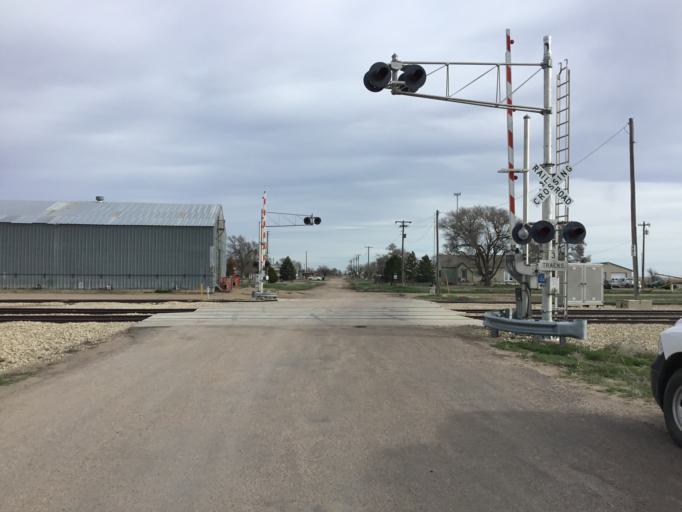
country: US
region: Colorado
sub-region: Kit Carson County
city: Burlington
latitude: 39.3334
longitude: -102.0329
